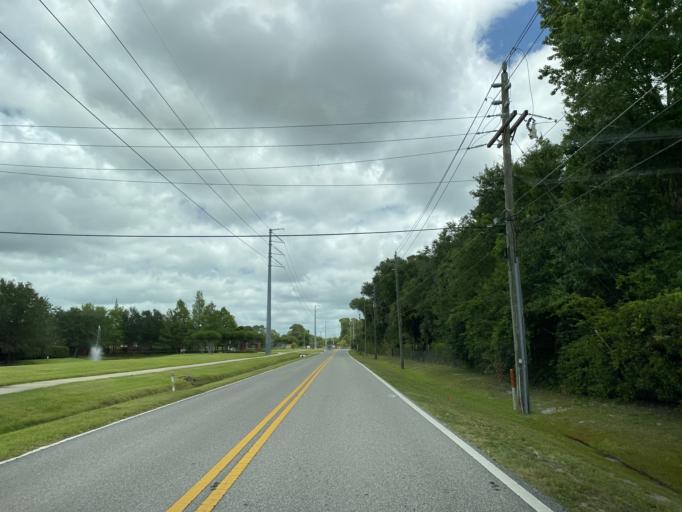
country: US
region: Florida
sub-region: Volusia County
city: DeBary
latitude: 28.8257
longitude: -81.3393
